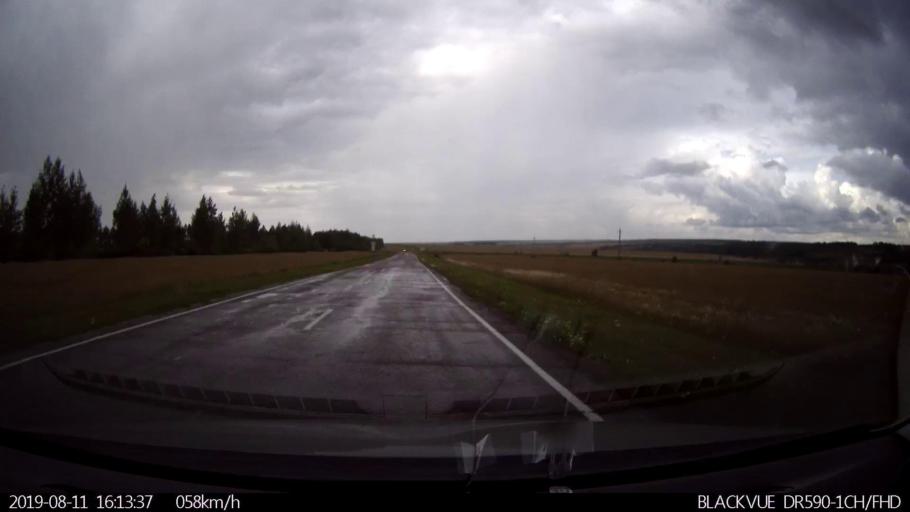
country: RU
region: Ulyanovsk
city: Ignatovka
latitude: 54.0215
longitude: 47.6363
